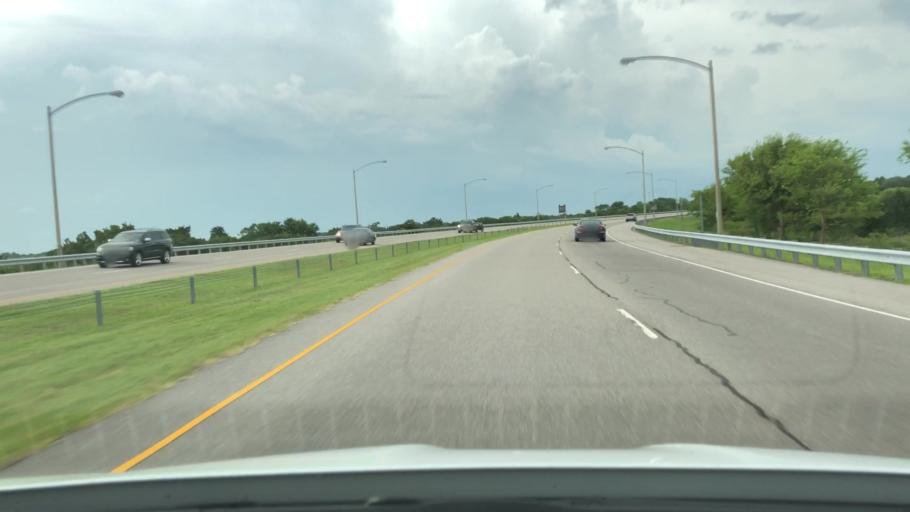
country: US
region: Virginia
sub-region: Northampton County
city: Cape Charles
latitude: 37.0979
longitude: -75.9694
